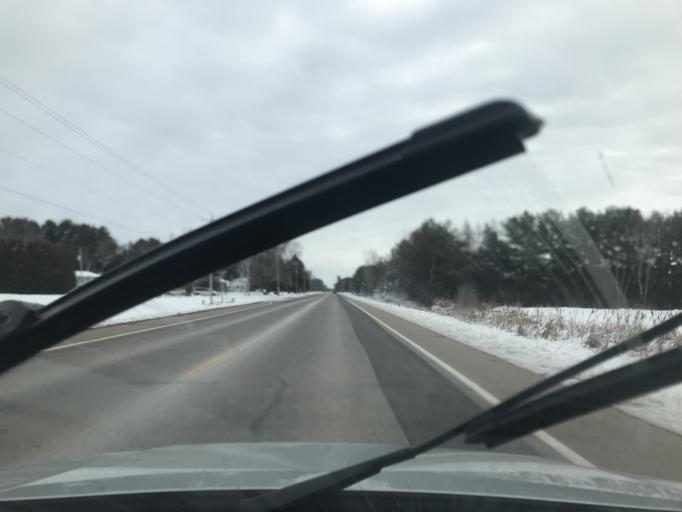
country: US
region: Wisconsin
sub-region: Marinette County
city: Marinette
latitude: 45.0999
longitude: -87.6830
